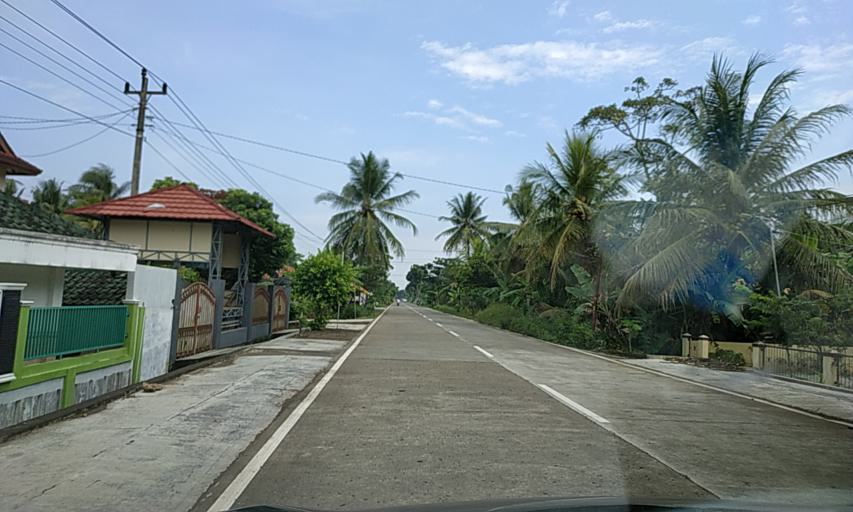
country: ID
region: Central Java
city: Tambangan
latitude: -7.4832
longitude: 108.8334
